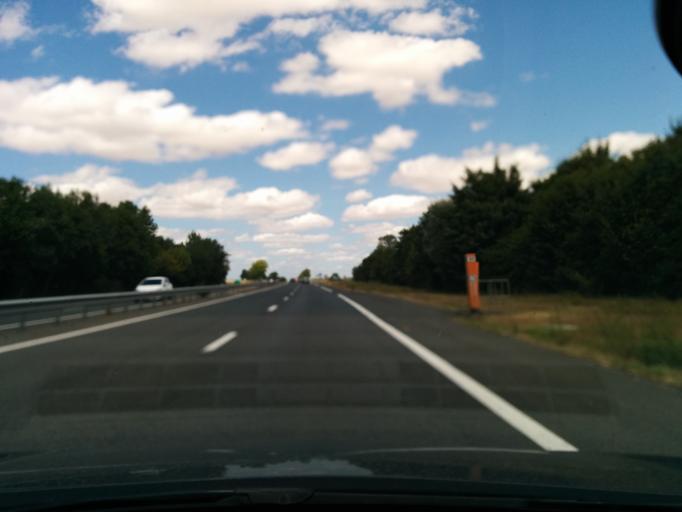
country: FR
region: Centre
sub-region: Departement de l'Indre
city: Montierchaume
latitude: 46.8849
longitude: 1.7263
